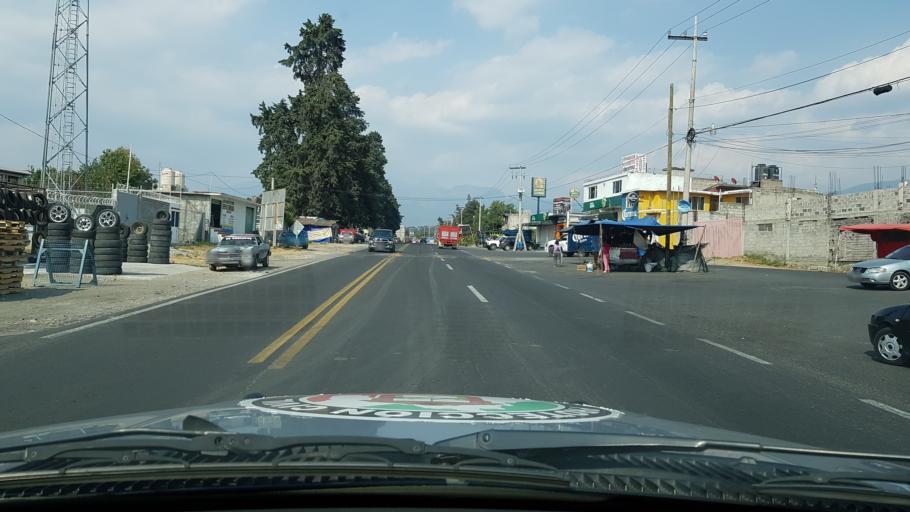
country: MX
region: Mexico
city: Ozumba de Alzate
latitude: 19.0444
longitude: -98.7975
